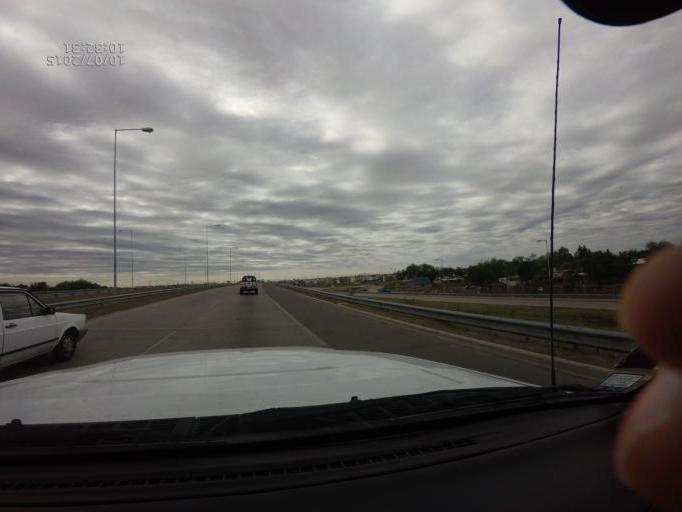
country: AR
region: Cordoba
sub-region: Departamento de Capital
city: Cordoba
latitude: -31.3532
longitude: -64.2280
